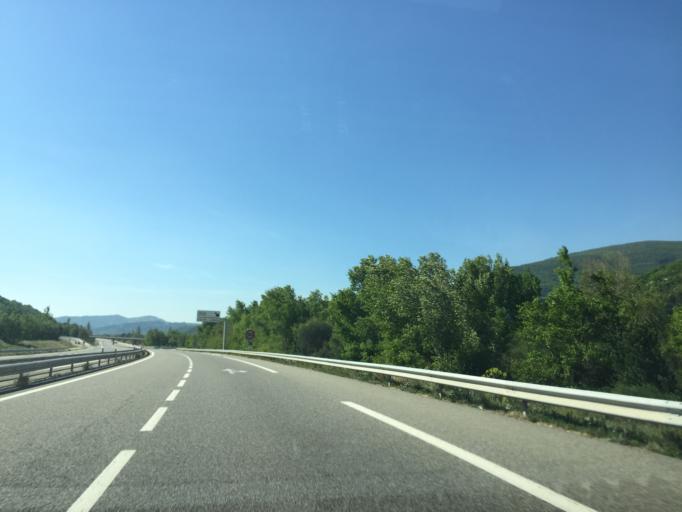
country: FR
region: Provence-Alpes-Cote d'Azur
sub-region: Departement des Alpes-de-Haute-Provence
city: Sisteron
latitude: 44.1739
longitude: 5.9537
